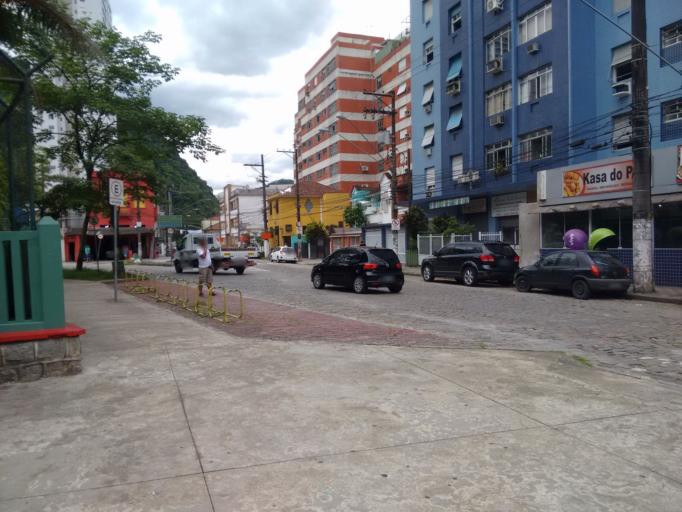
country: BR
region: Sao Paulo
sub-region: Santos
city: Santos
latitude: -23.9654
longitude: -46.3490
